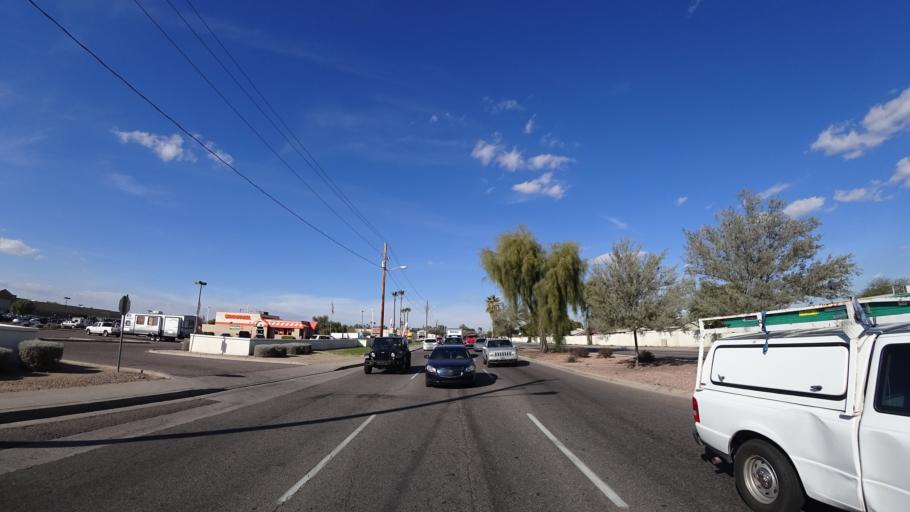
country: US
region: Arizona
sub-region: Maricopa County
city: Tolleson
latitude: 33.4700
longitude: -112.2208
